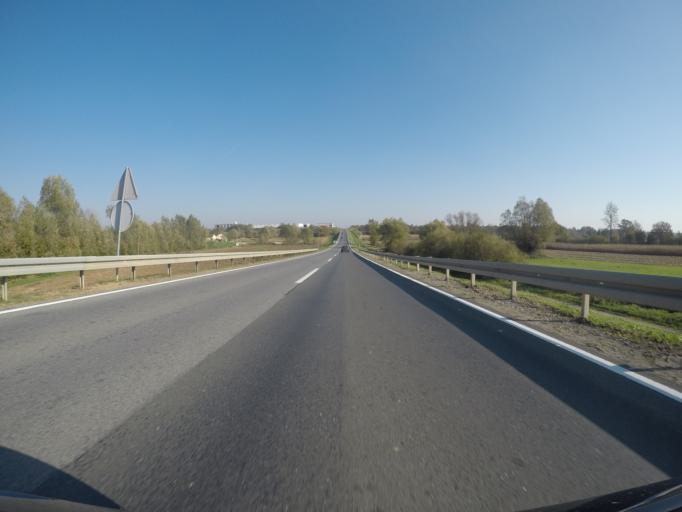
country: HR
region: Bjelovarsko-Bilogorska
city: Bjelovar
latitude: 45.9306
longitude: 16.8313
